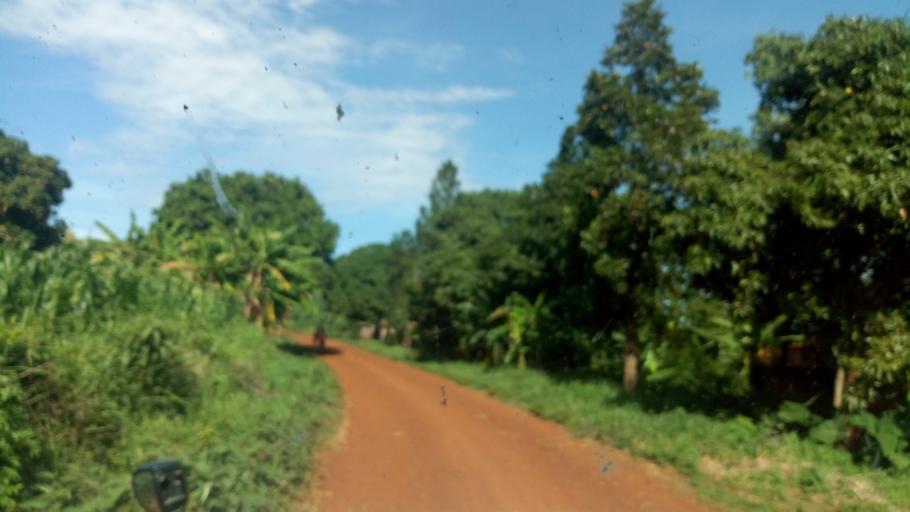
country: UG
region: Western Region
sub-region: Masindi District
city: Masindi
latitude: 1.6406
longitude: 31.7569
